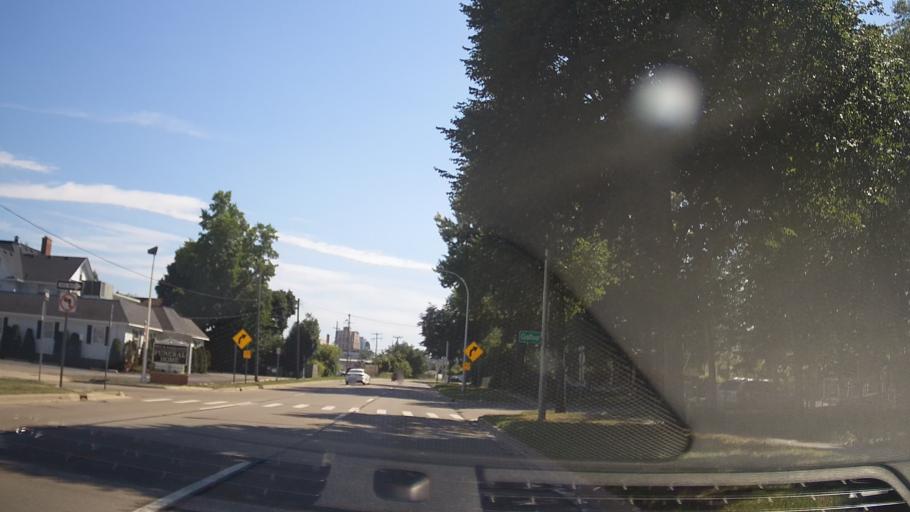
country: US
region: Michigan
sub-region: Macomb County
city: Mount Clemens
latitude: 42.6052
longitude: -82.8745
